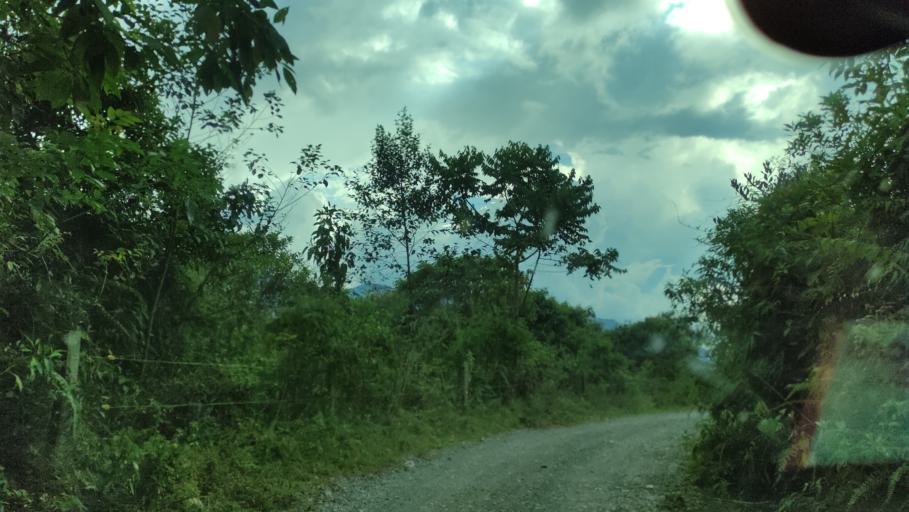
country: CO
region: Valle del Cauca
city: San Pedro
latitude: 3.8769
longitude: -76.1488
